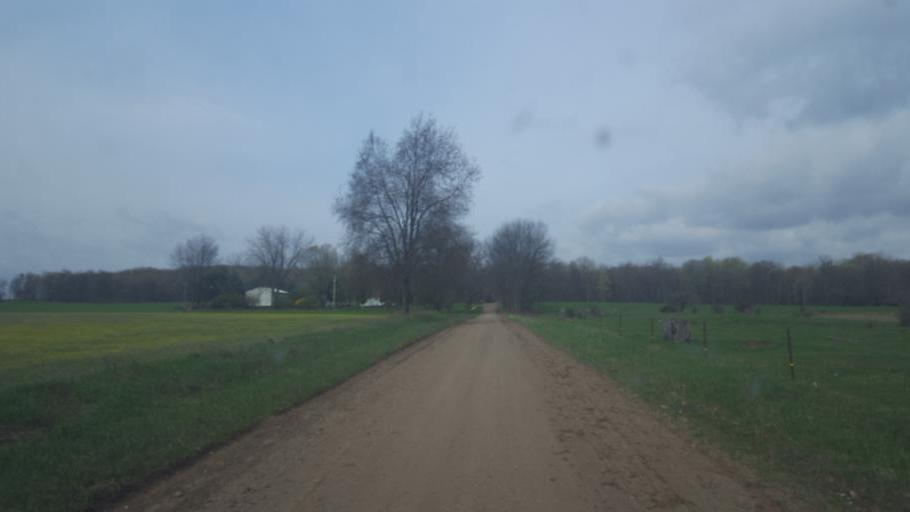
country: US
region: Michigan
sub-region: Isabella County
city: Lake Isabella
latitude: 43.5178
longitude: -84.9295
